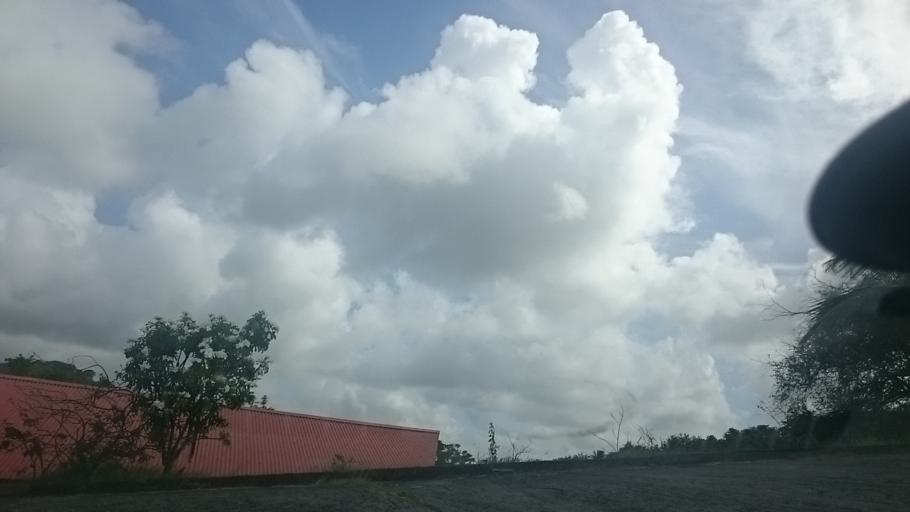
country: MQ
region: Martinique
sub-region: Martinique
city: Le Francois
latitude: 14.6064
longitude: -60.8973
